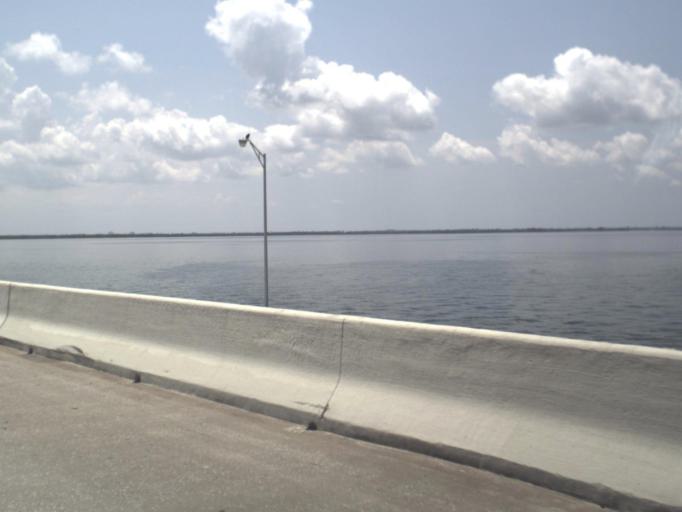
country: US
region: Florida
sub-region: Manatee County
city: Memphis
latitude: 27.5931
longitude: -82.6311
